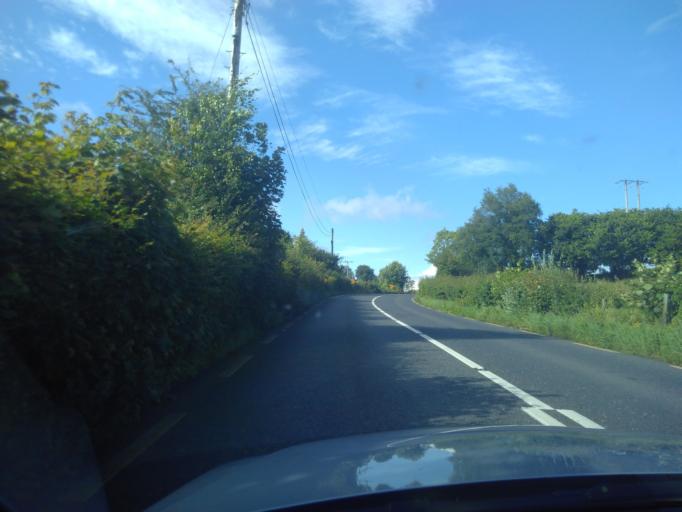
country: IE
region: Ulster
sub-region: County Donegal
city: Ballybofey
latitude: 54.8194
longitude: -7.7567
